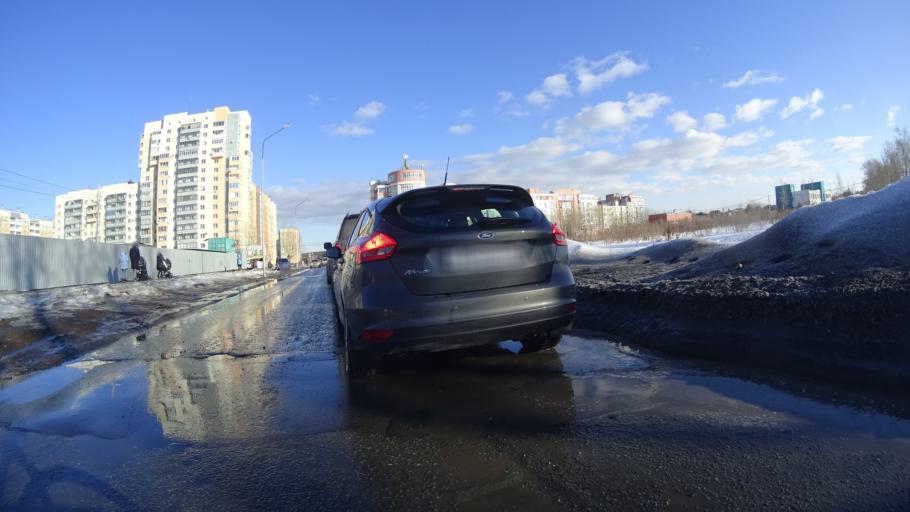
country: RU
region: Chelyabinsk
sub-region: Gorod Chelyabinsk
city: Chelyabinsk
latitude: 55.1600
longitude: 61.2952
